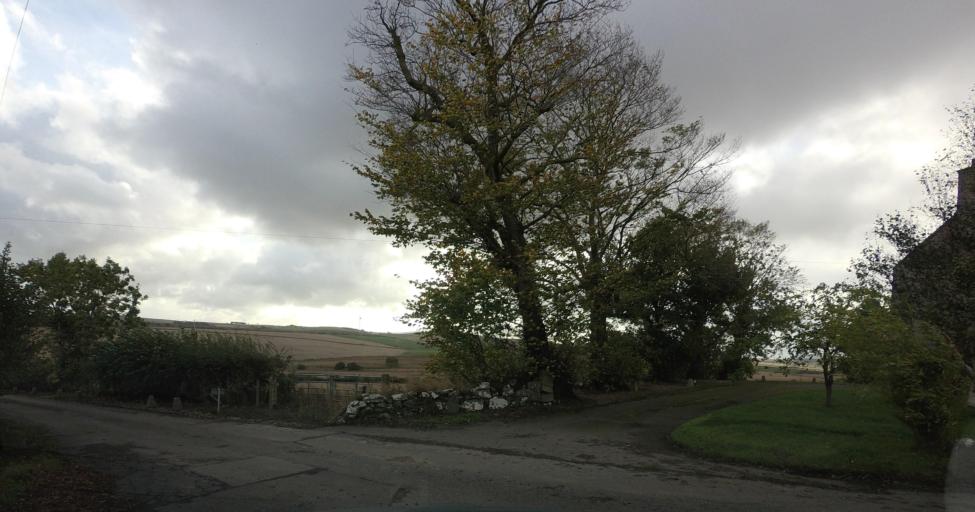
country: GB
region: Scotland
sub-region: Aberdeenshire
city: Whitehills
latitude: 57.6556
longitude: -2.6151
